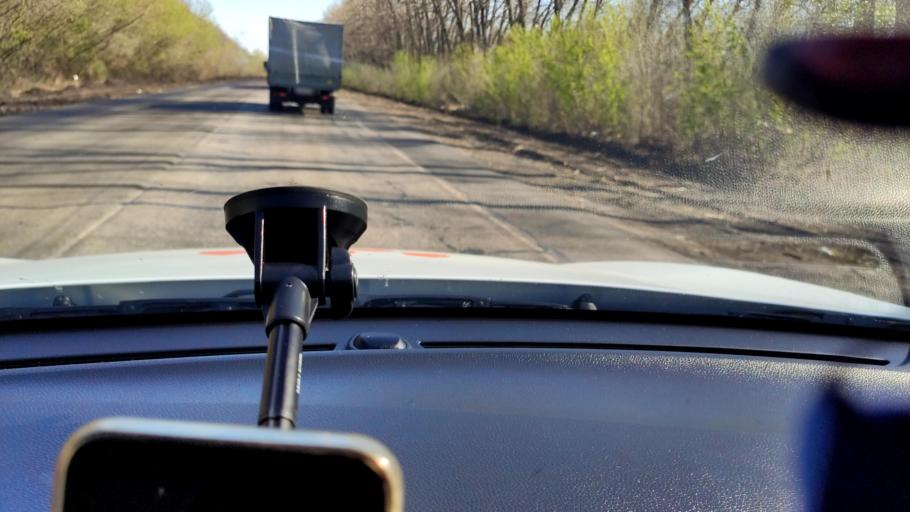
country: RU
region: Voronezj
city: Uryv-Pokrovka
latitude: 51.1964
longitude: 39.0837
